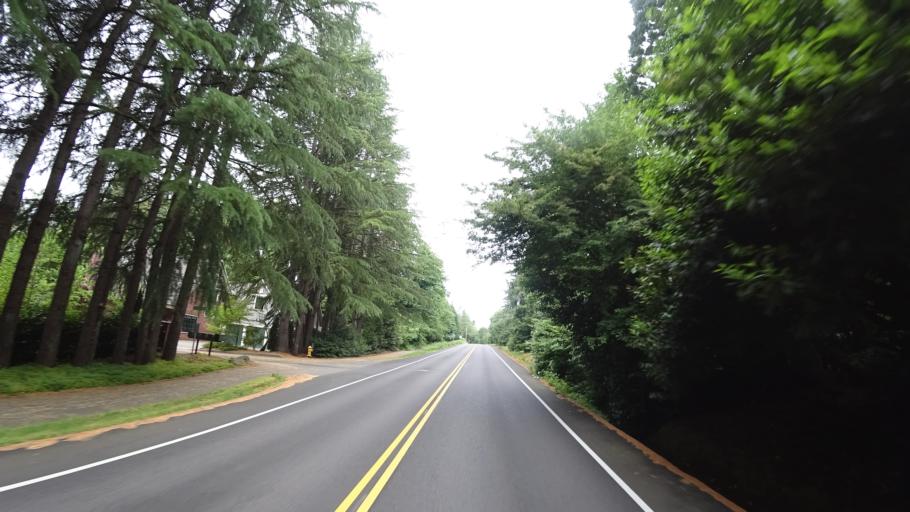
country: US
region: Oregon
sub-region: Clackamas County
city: Lake Oswego
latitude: 45.4329
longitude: -122.6664
